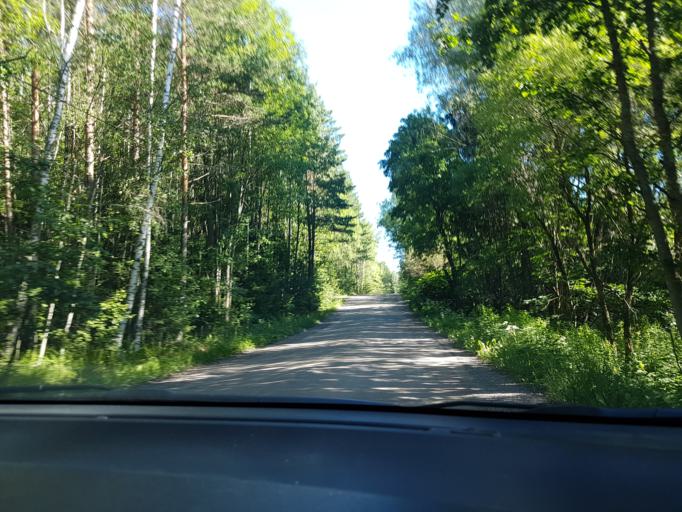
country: FI
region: Uusimaa
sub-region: Helsinki
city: Sibbo
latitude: 60.2739
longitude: 25.2343
